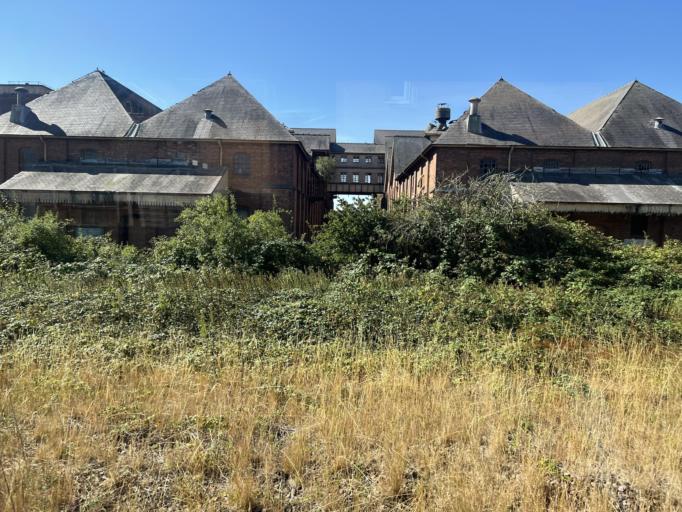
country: GB
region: England
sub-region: Lincolnshire
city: Sleaford
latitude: 52.9946
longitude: -0.4015
